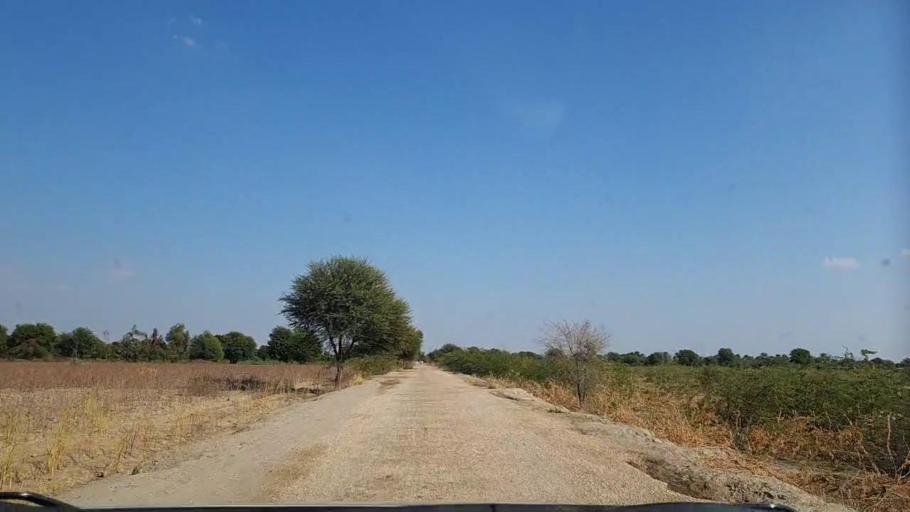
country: PK
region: Sindh
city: Pithoro
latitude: 25.6347
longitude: 69.3554
